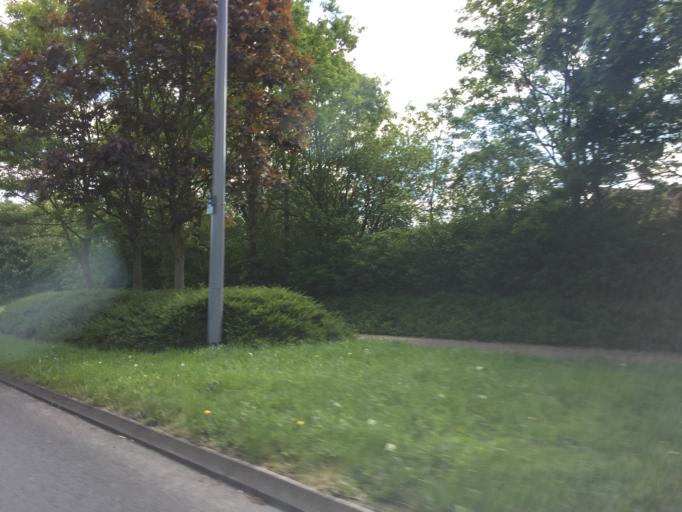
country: GB
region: England
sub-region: Milton Keynes
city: Milton Keynes
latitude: 52.0334
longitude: -0.7490
